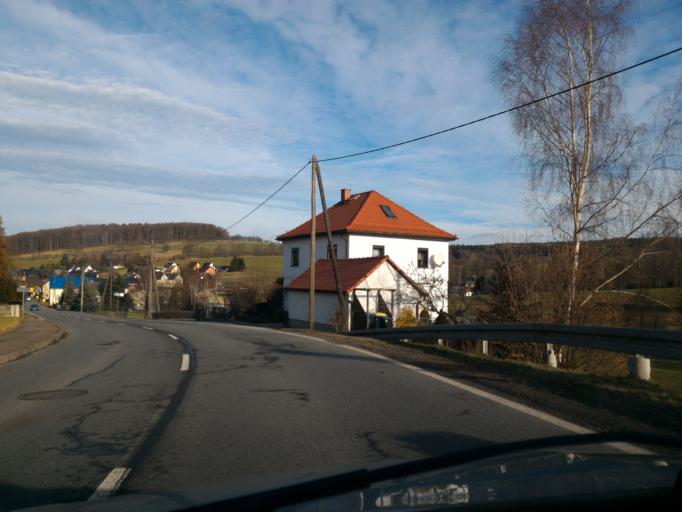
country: DE
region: Saxony
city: Steinigtwolmsdorf
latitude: 51.0734
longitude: 14.3411
